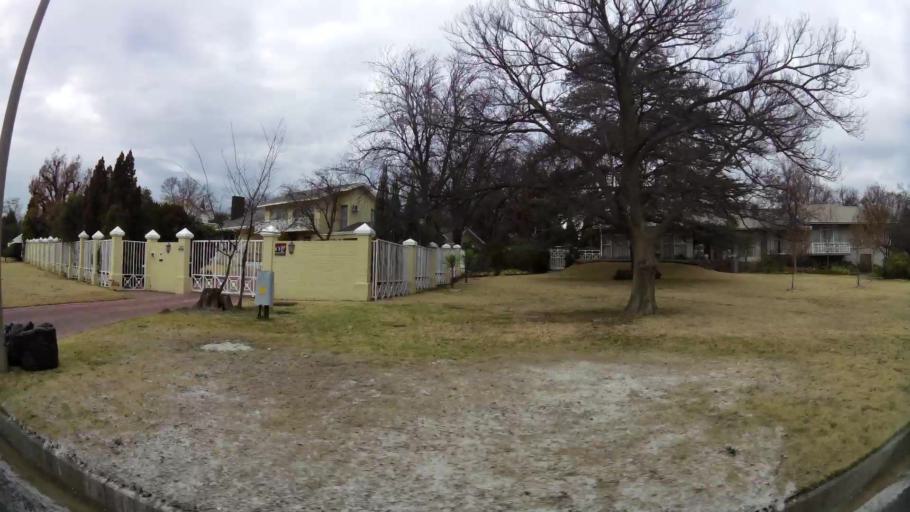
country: ZA
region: Orange Free State
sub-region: Fezile Dabi District Municipality
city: Kroonstad
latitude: -27.6694
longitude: 27.2465
